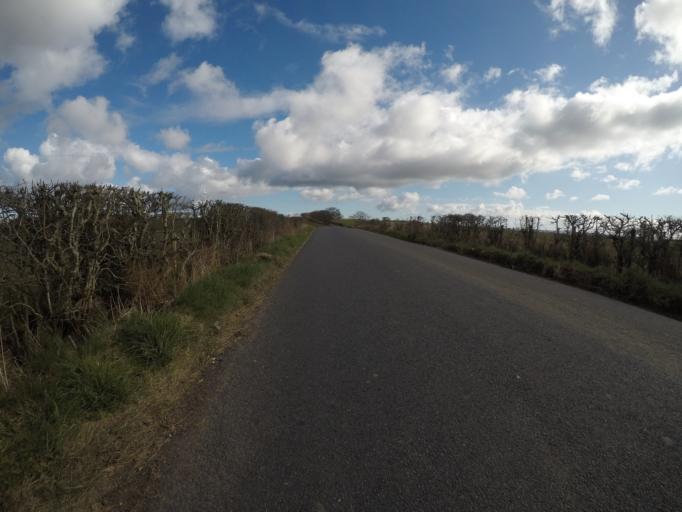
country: GB
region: Scotland
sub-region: North Ayrshire
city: Kilwinning
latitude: 55.6757
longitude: -4.6579
